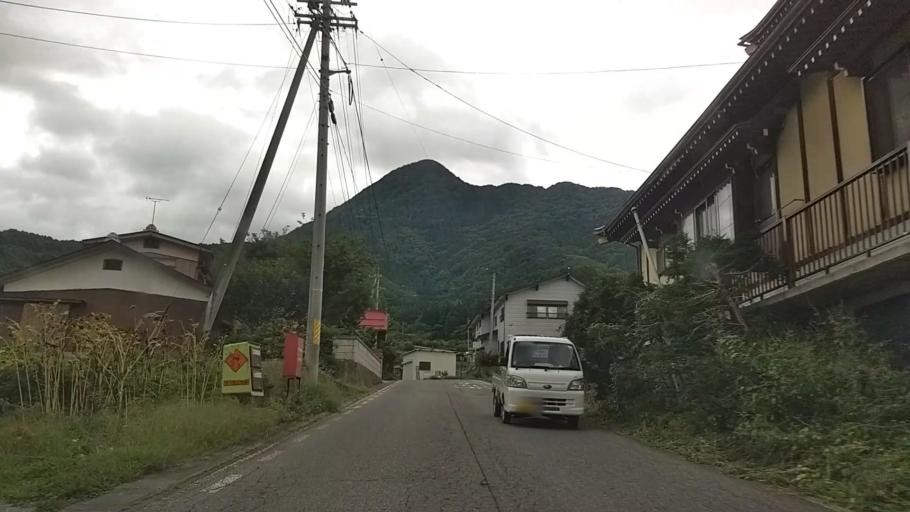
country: JP
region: Nagano
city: Iiyama
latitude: 36.8174
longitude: 138.3636
